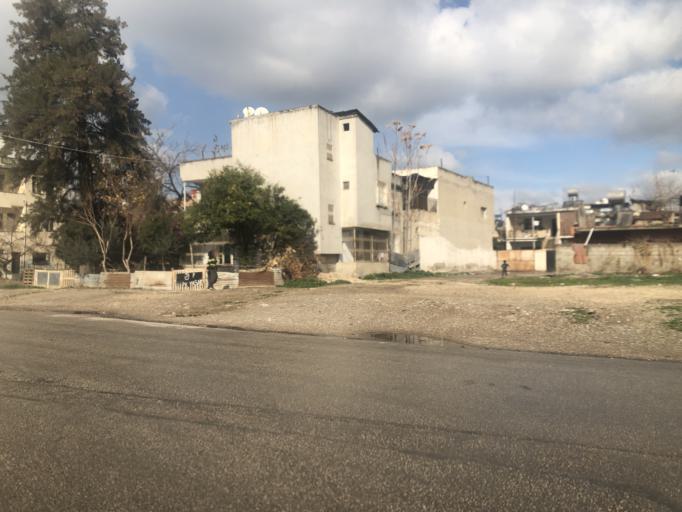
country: TR
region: Adana
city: Adana
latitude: 36.9912
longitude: 35.3420
